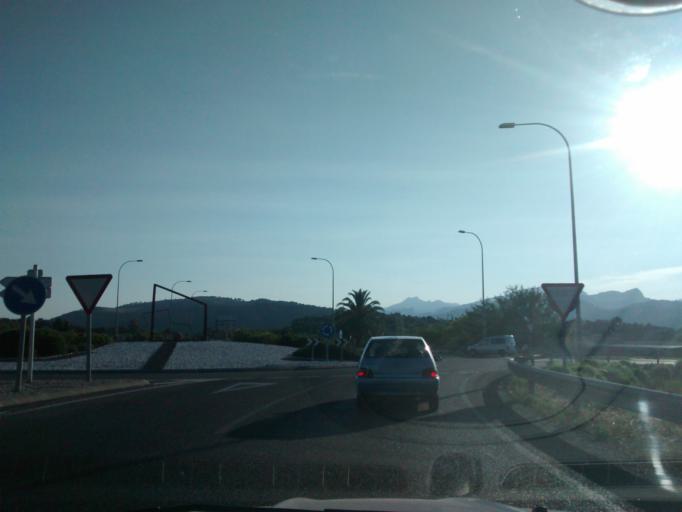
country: ES
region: Balearic Islands
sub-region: Illes Balears
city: Alcudia
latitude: 39.8416
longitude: 3.0819
